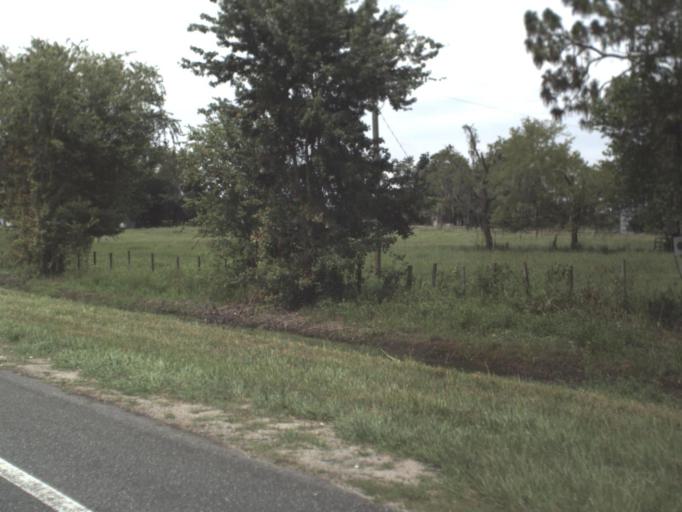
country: US
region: Florida
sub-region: Suwannee County
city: Live Oak
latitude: 30.2110
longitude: -82.9880
